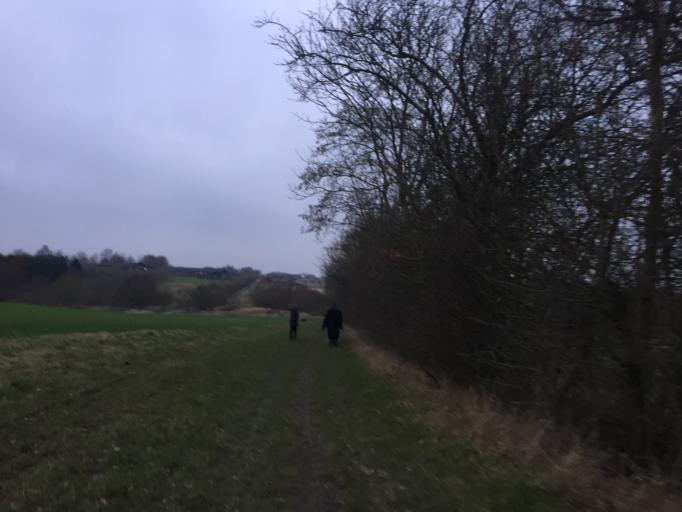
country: DK
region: South Denmark
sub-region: Kolding Kommune
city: Sonder Bjert
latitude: 55.4545
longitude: 9.5642
